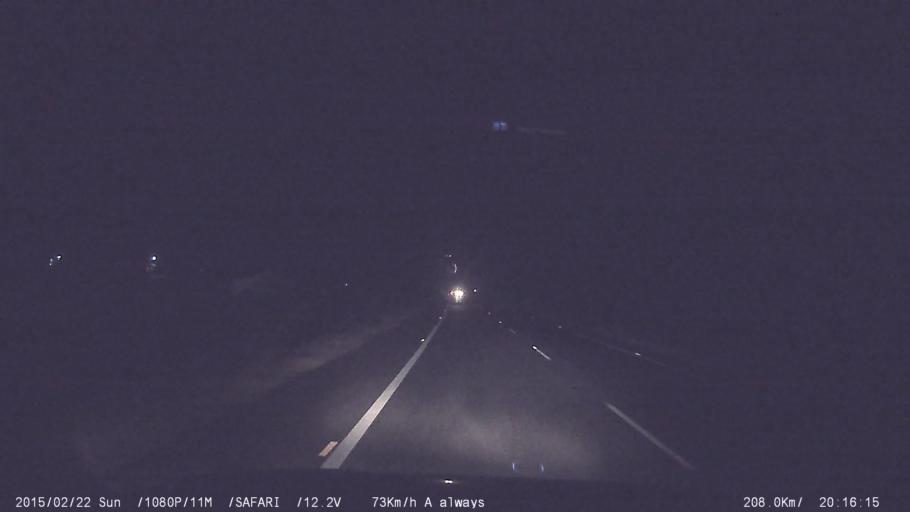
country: IN
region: Tamil Nadu
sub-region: Dindigul
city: Nilakottai
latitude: 10.2644
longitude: 77.8486
